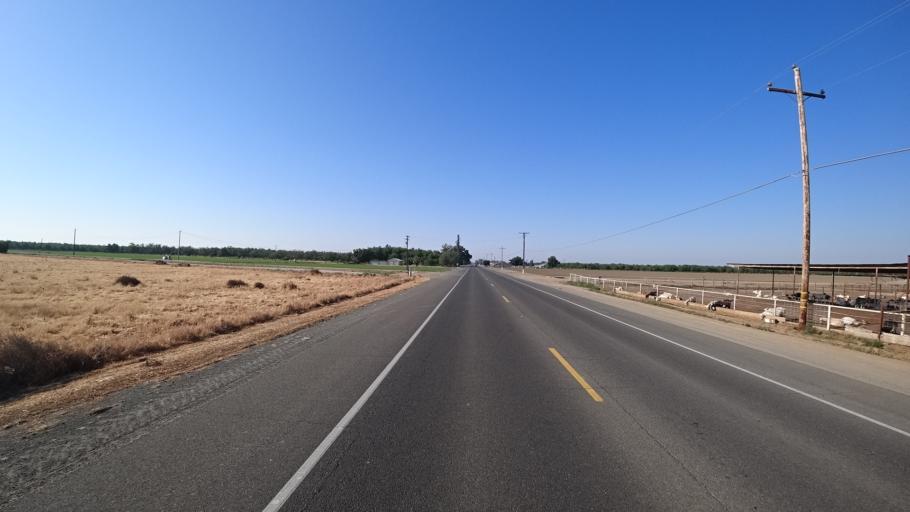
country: US
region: California
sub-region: Kings County
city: Armona
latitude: 36.3366
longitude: -119.7090
